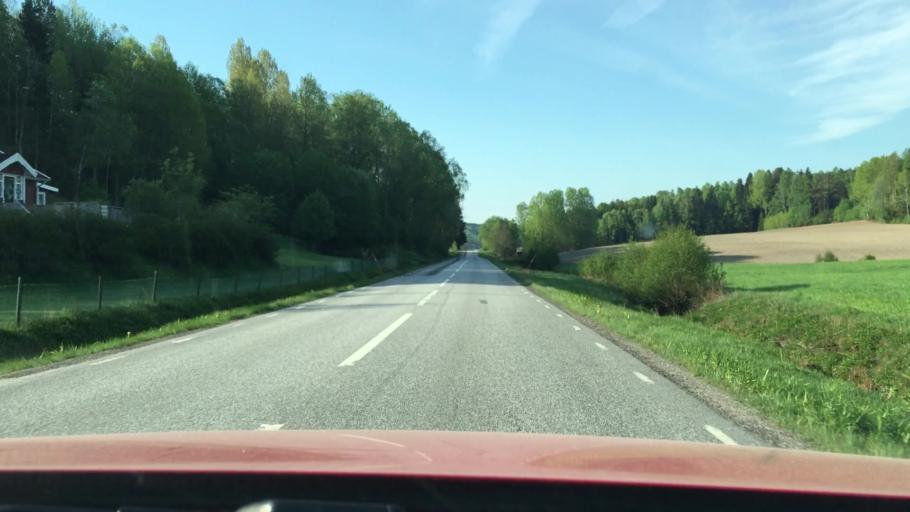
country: SE
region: Vaestra Goetaland
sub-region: Munkedals Kommun
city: Munkedal
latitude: 58.6178
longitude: 11.5585
